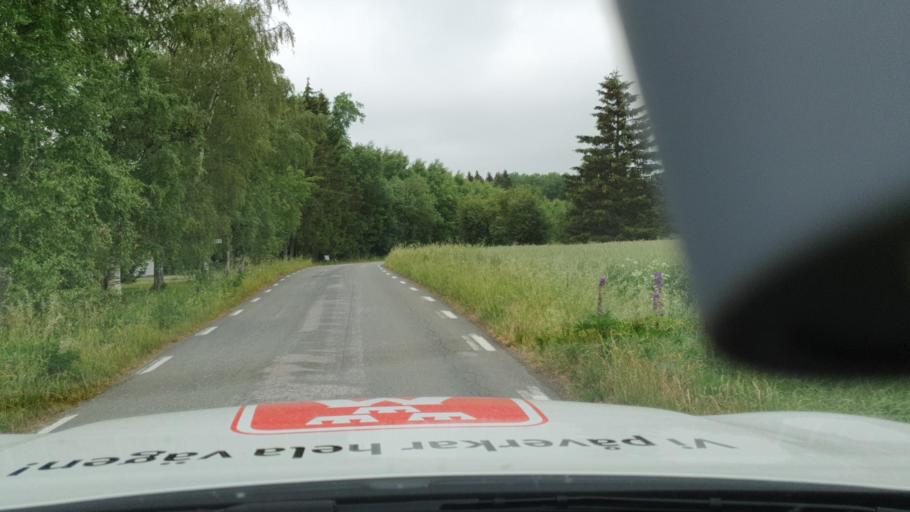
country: SE
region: Vaestra Goetaland
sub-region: Tidaholms Kommun
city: Olofstorp
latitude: 58.3766
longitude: 14.0045
